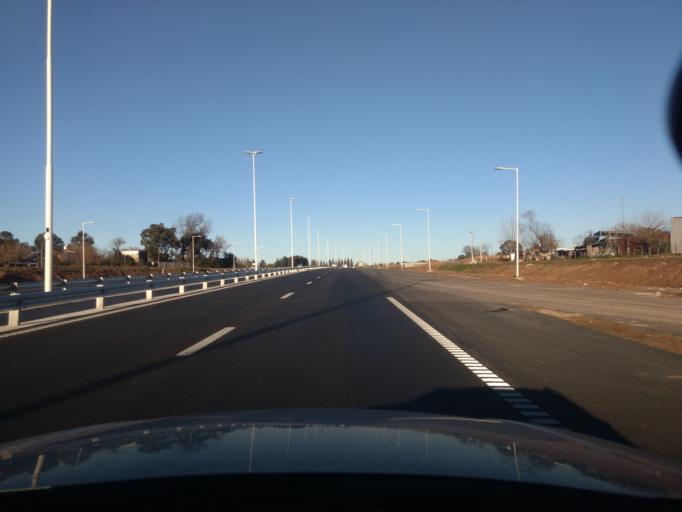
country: AR
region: Buenos Aires
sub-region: Partido de Lujan
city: Lujan
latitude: -34.5823
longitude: -59.0879
